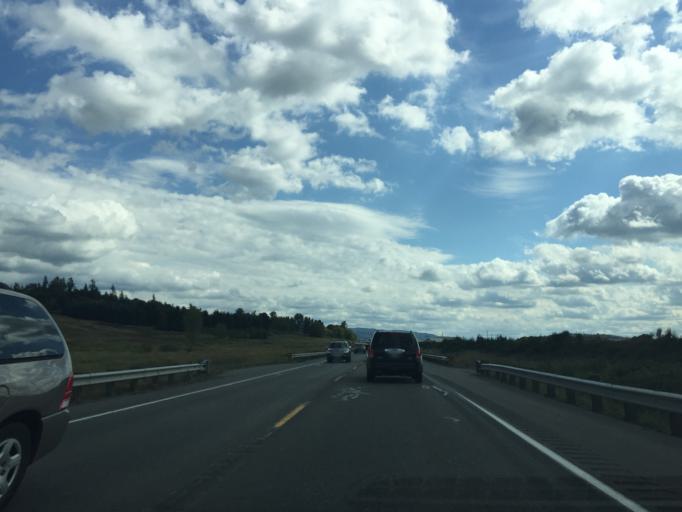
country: US
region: Washington
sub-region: Snohomish County
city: Monroe
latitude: 47.8810
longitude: -122.0202
